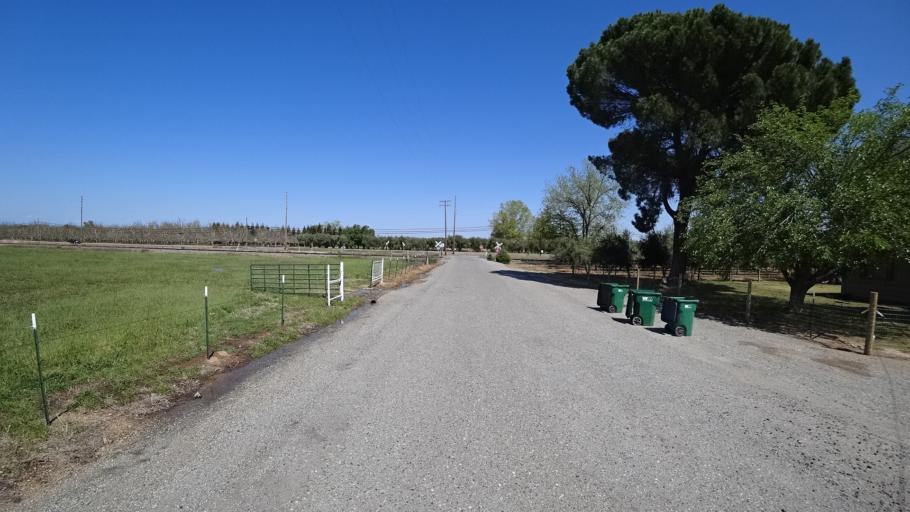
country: US
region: California
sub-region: Glenn County
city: Orland
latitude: 39.7681
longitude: -122.1682
